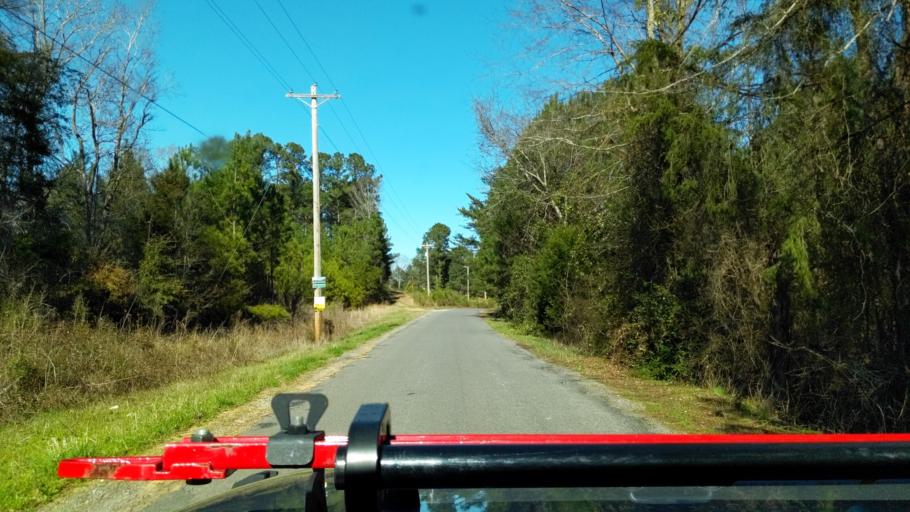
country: US
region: Alabama
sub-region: Walker County
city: Jasper
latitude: 34.0528
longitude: -87.1536
